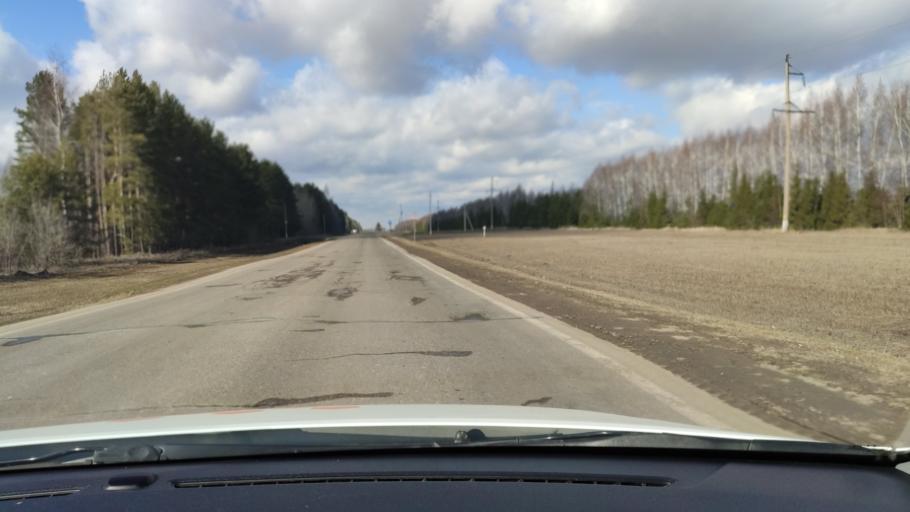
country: RU
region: Tatarstan
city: Vysokaya Gora
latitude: 56.0598
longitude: 49.2059
